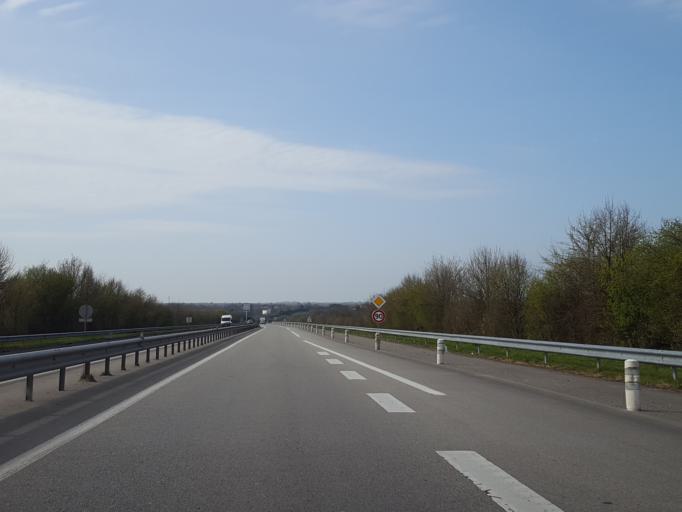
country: FR
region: Pays de la Loire
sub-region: Departement de la Vendee
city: La Roche-sur-Yon
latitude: 46.6780
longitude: -1.4532
